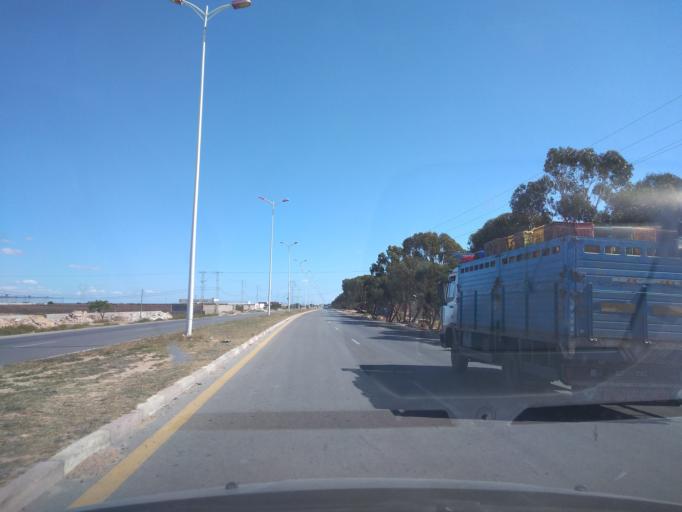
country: TN
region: Safaqis
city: Sfax
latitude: 34.8171
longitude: 10.7019
